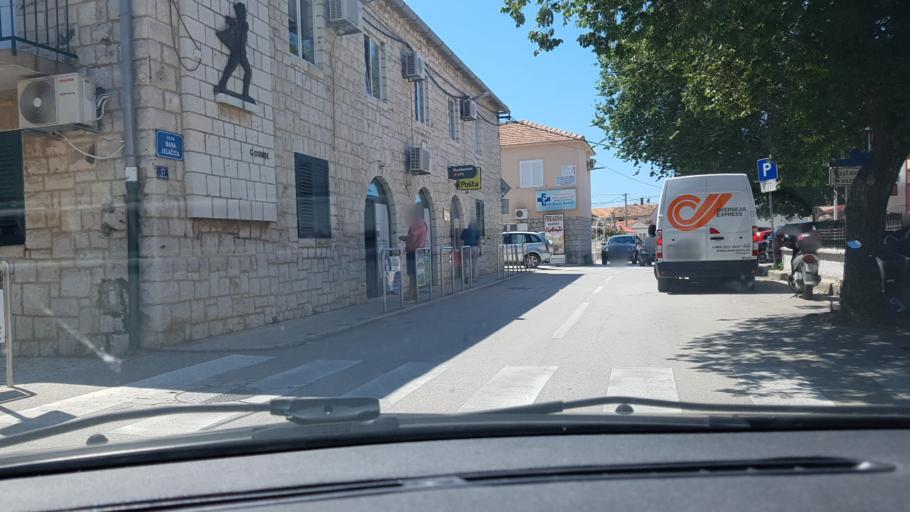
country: HR
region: Splitsko-Dalmatinska
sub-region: Grad Trogir
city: Trogir
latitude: 43.4936
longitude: 16.2641
